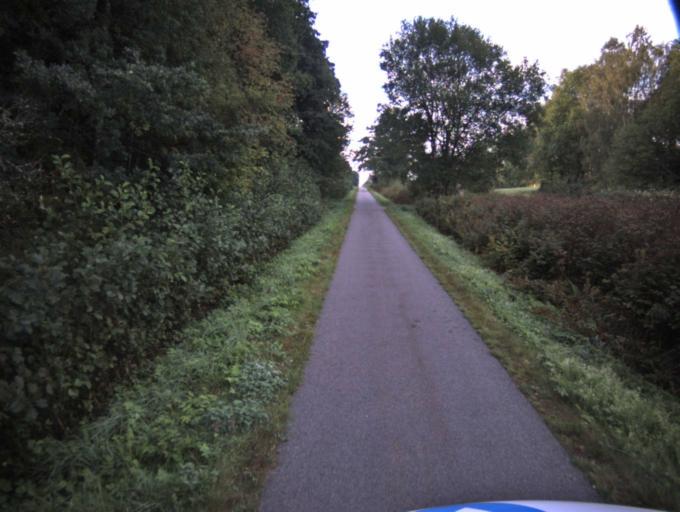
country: SE
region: Vaestra Goetaland
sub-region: Ulricehamns Kommun
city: Ulricehamn
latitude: 57.7679
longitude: 13.4011
